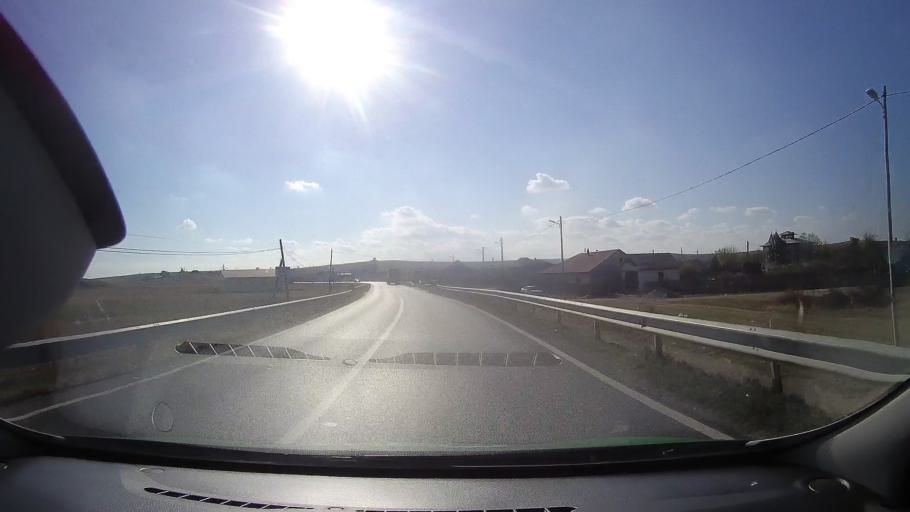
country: RO
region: Tulcea
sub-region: Comuna Baia
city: Baia
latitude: 44.7228
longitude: 28.6795
